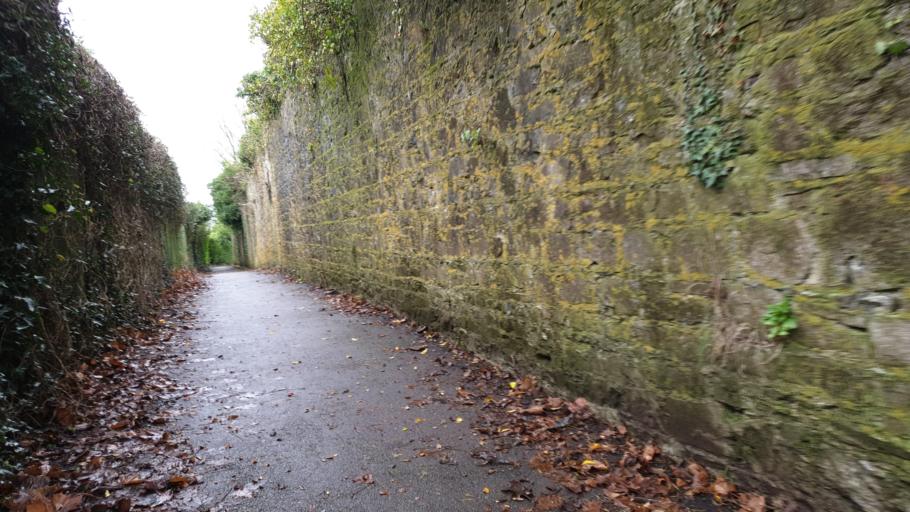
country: IE
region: Munster
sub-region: County Cork
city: Cork
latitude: 51.8893
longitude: -8.4321
